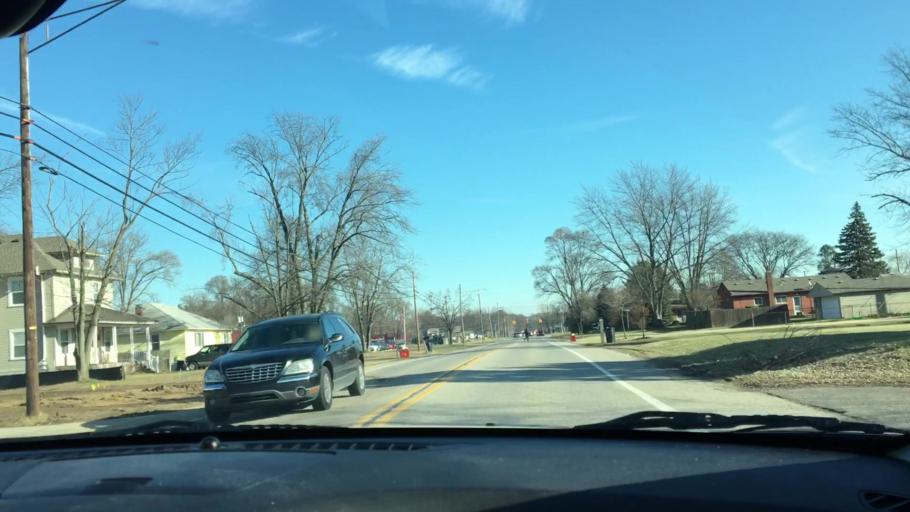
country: US
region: Michigan
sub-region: Wayne County
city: Westland
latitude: 42.3560
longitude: -83.3907
